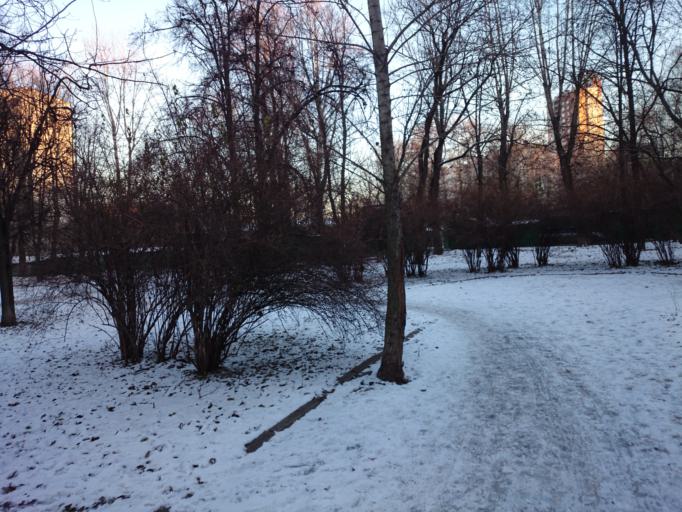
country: RU
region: Moscow
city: Sokol
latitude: 55.7949
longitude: 37.5182
